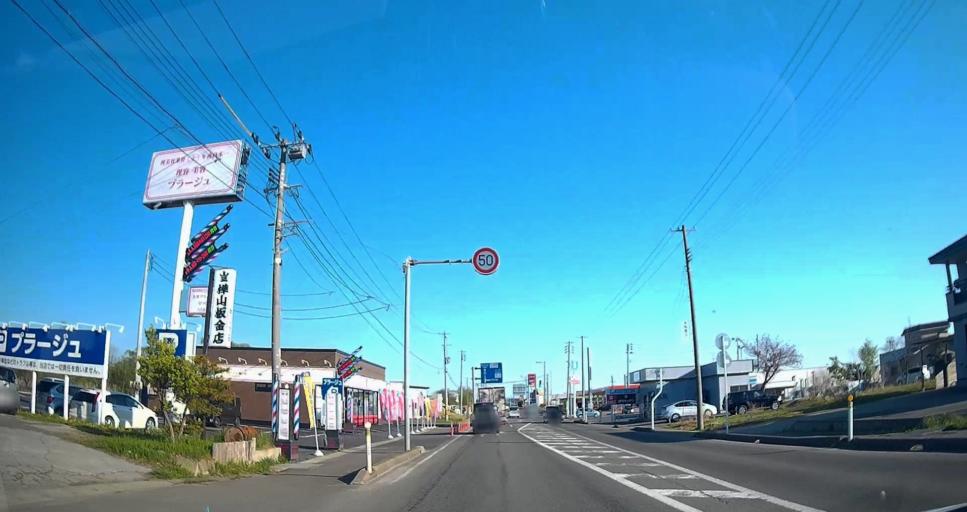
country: JP
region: Aomori
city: Mutsu
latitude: 41.3060
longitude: 141.2196
